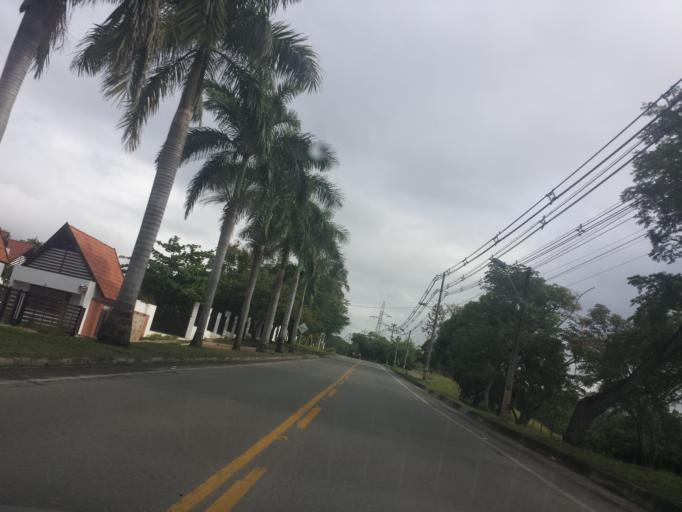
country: CO
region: Antioquia
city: Antioquia
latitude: 6.5442
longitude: -75.8200
